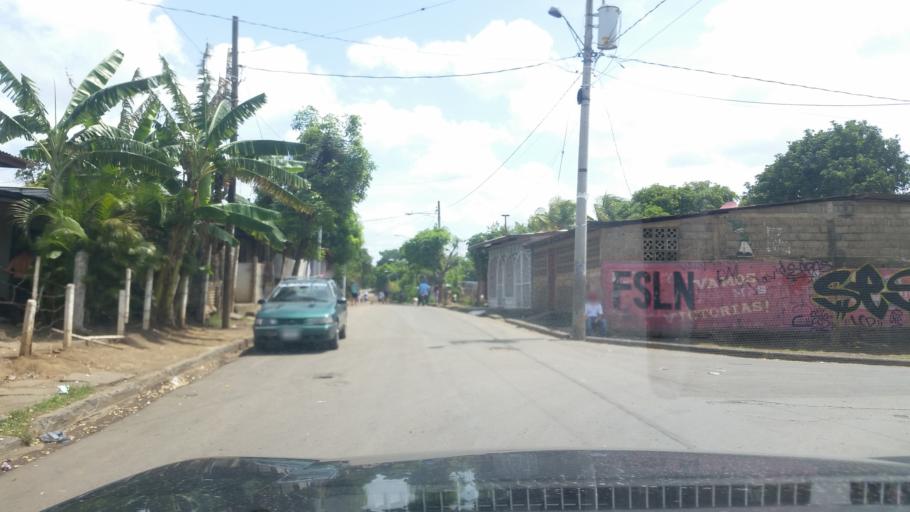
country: NI
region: Managua
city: Managua
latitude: 12.1078
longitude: -86.2374
